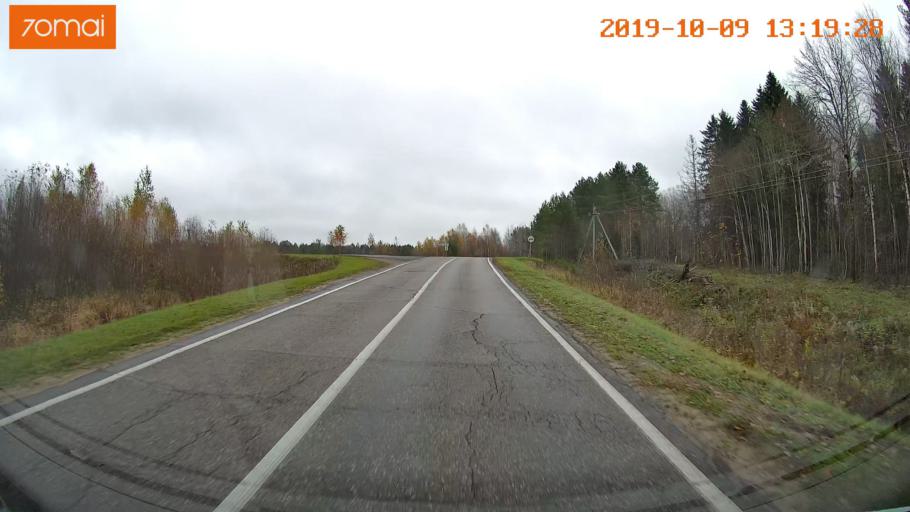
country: RU
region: Jaroslavl
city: Lyubim
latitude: 58.3494
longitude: 40.8140
